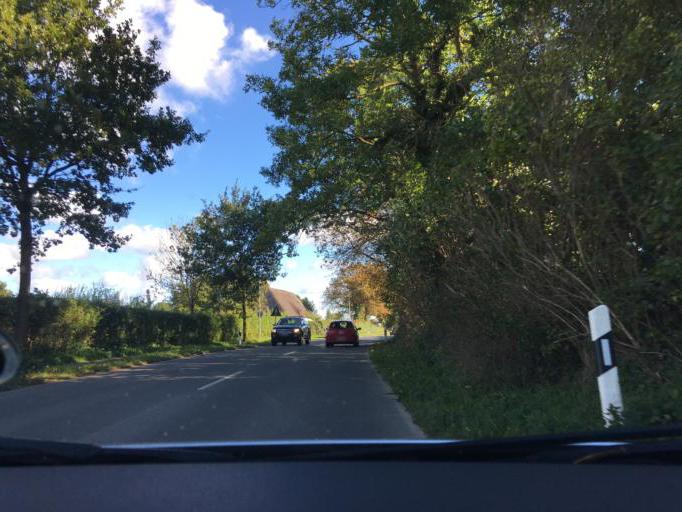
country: DE
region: Schleswig-Holstein
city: Ottendorf
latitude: 54.3397
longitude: 10.0609
